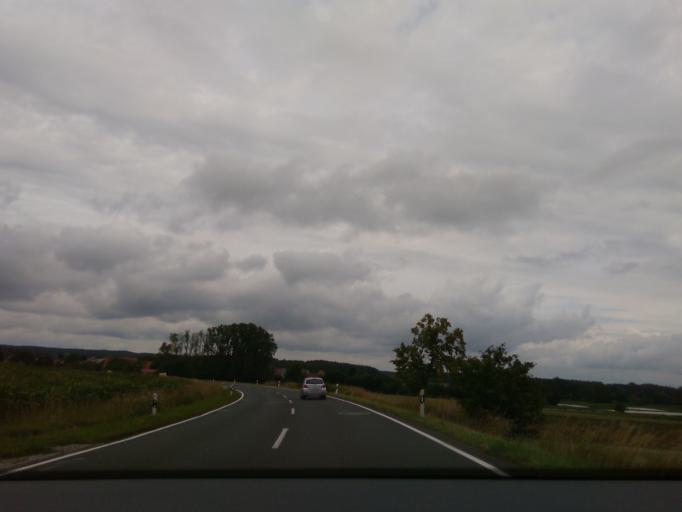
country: DE
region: Bavaria
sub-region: Regierungsbezirk Mittelfranken
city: Weisendorf
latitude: 49.6294
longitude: 10.8236
